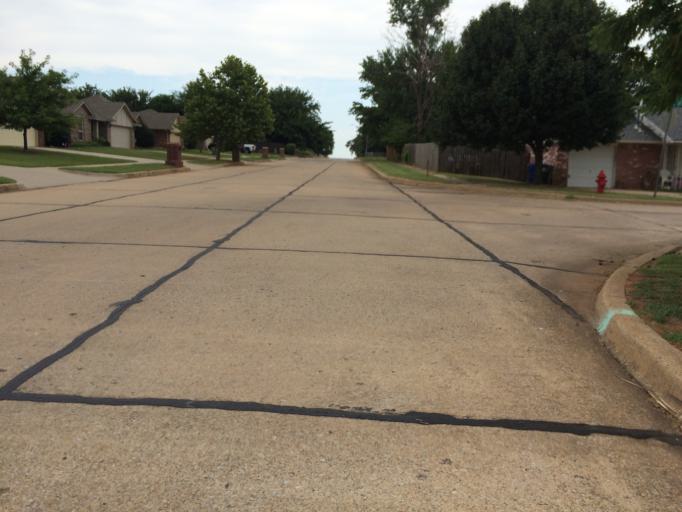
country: US
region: Oklahoma
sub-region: Cleveland County
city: Hall Park
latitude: 35.2505
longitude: -97.4190
